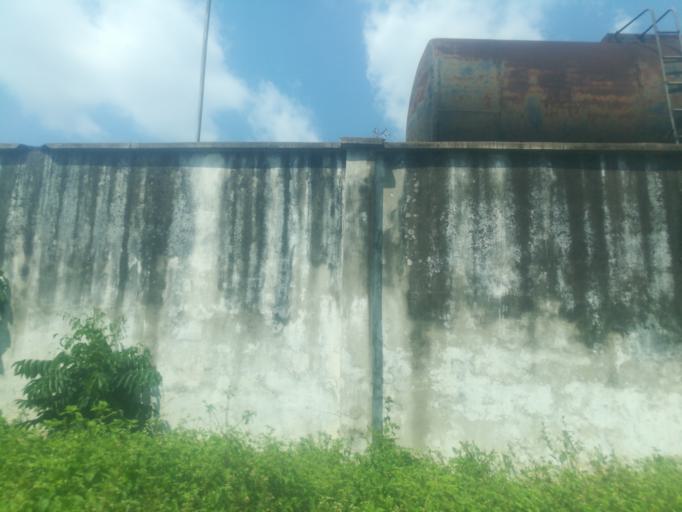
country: NG
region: Oyo
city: Moniya
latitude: 7.5117
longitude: 3.9132
